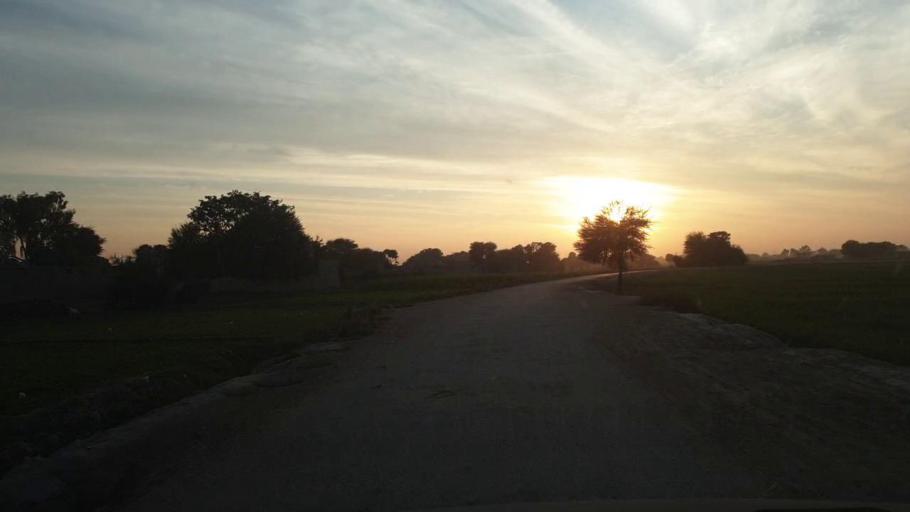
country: PK
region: Sindh
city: Shahpur Chakar
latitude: 26.0775
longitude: 68.5322
